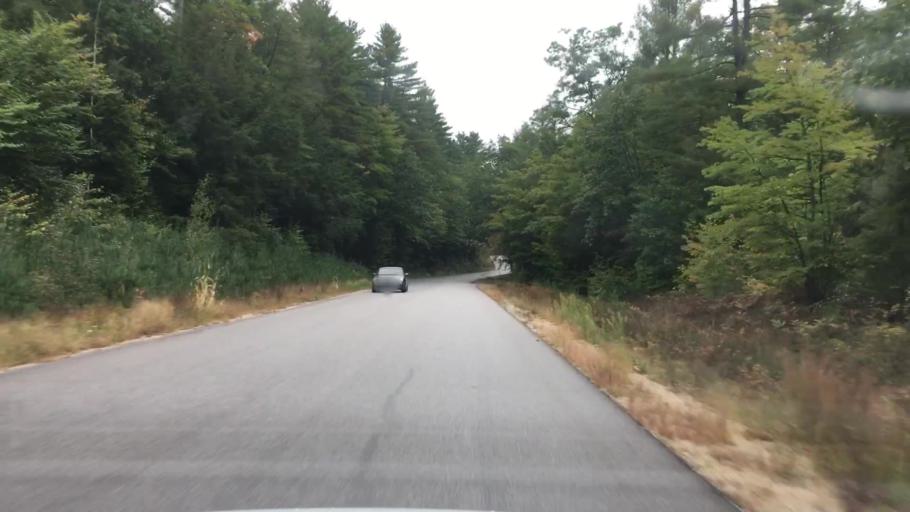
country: US
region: Maine
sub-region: Cumberland County
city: Harrison
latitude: 44.0301
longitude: -70.5969
